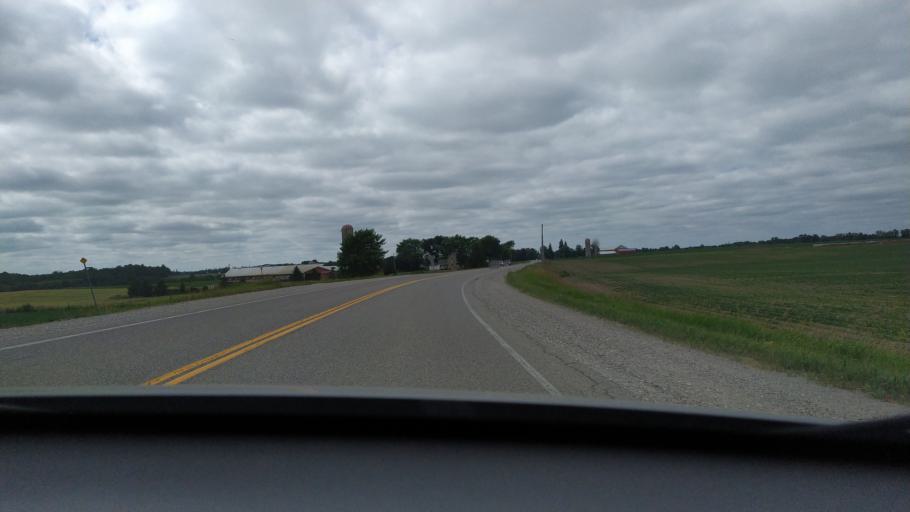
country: CA
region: Ontario
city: Stratford
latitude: 43.2833
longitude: -80.9659
